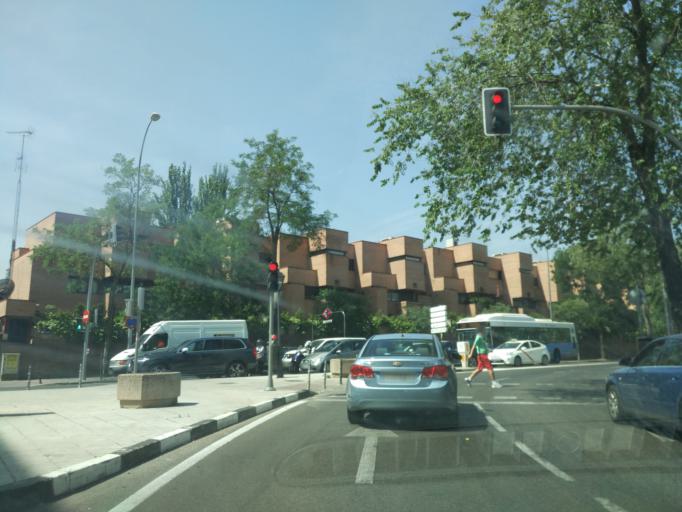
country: ES
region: Madrid
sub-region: Provincia de Madrid
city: Chamartin
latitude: 40.4678
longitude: -3.6790
